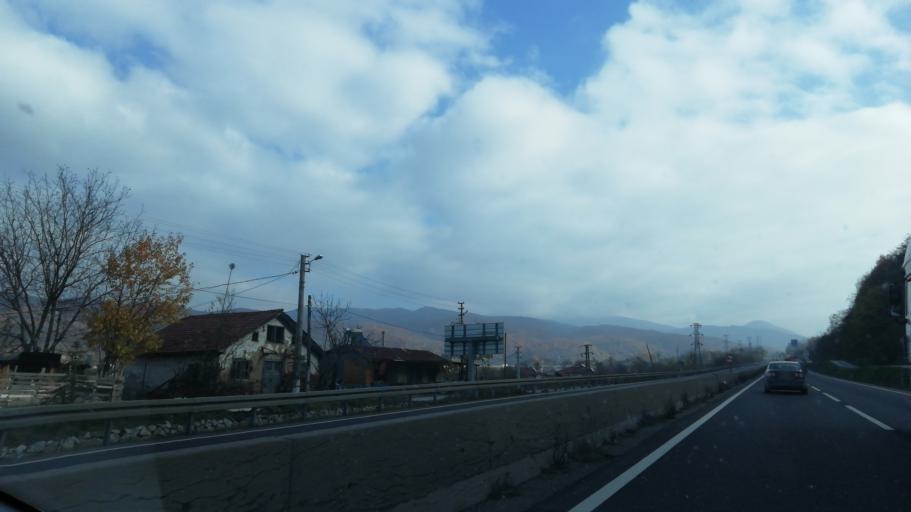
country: TR
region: Duzce
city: Kaynasli
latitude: 40.7723
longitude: 31.3348
